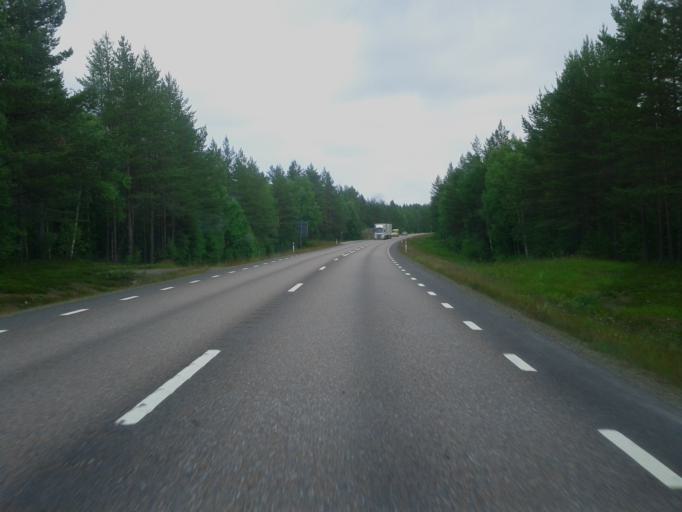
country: SE
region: Vaesterbotten
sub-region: Skelleftea Kommun
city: Burea
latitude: 64.3312
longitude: 21.2031
